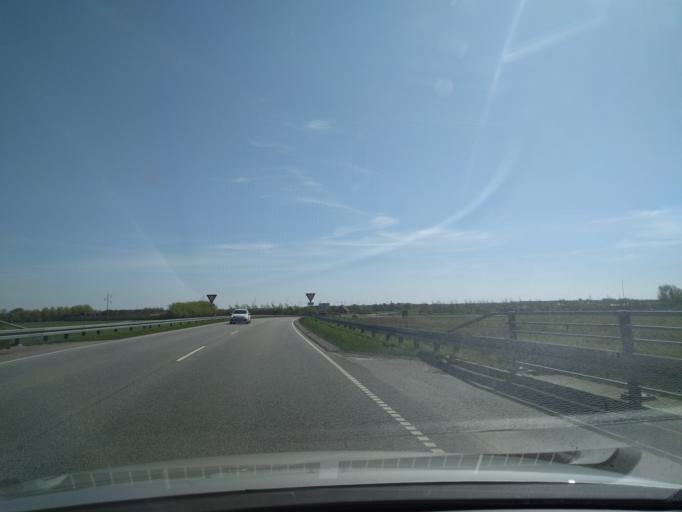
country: DK
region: Central Jutland
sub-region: Ringkobing-Skjern Kommune
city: Ringkobing
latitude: 56.1068
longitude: 8.2519
